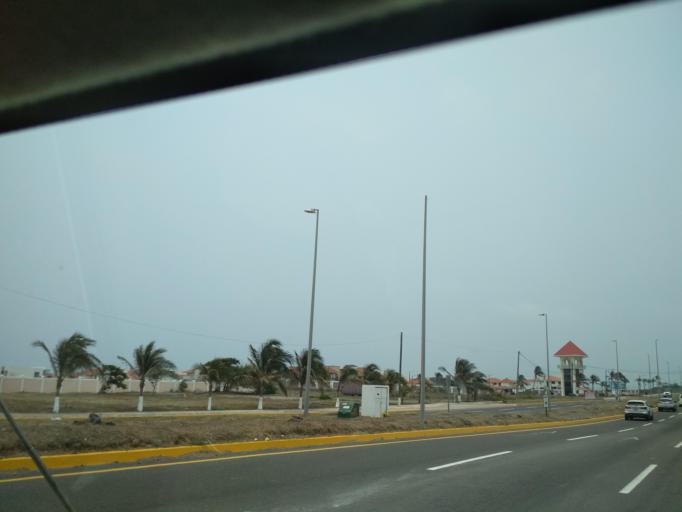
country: MX
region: Veracruz
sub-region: Alvarado
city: Playa de la Libertad
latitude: 19.0701
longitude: -96.0841
